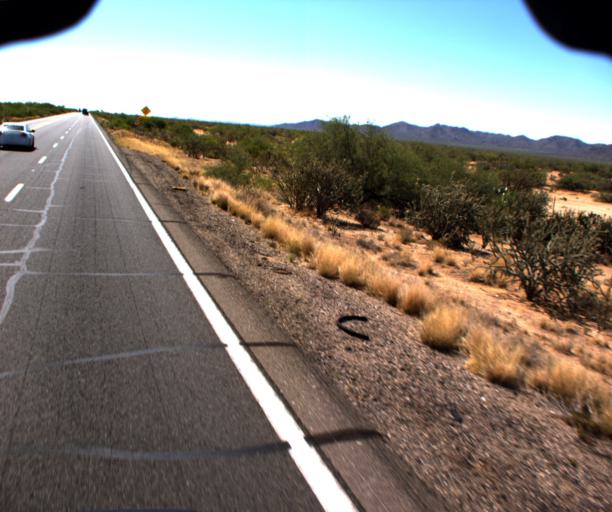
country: US
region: Arizona
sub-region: Yavapai County
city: Congress
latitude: 34.1470
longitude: -112.9846
